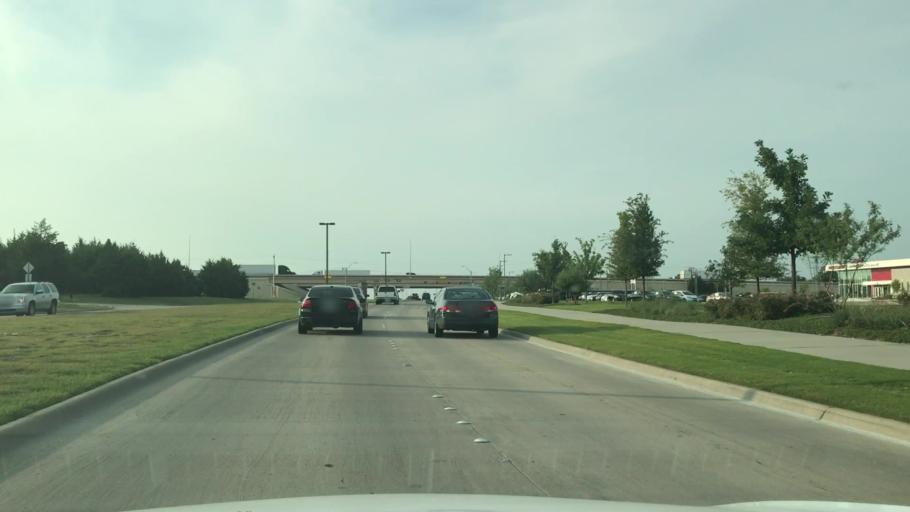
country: US
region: Texas
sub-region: Rockwall County
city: Rockwall
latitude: 32.9134
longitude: -96.4327
